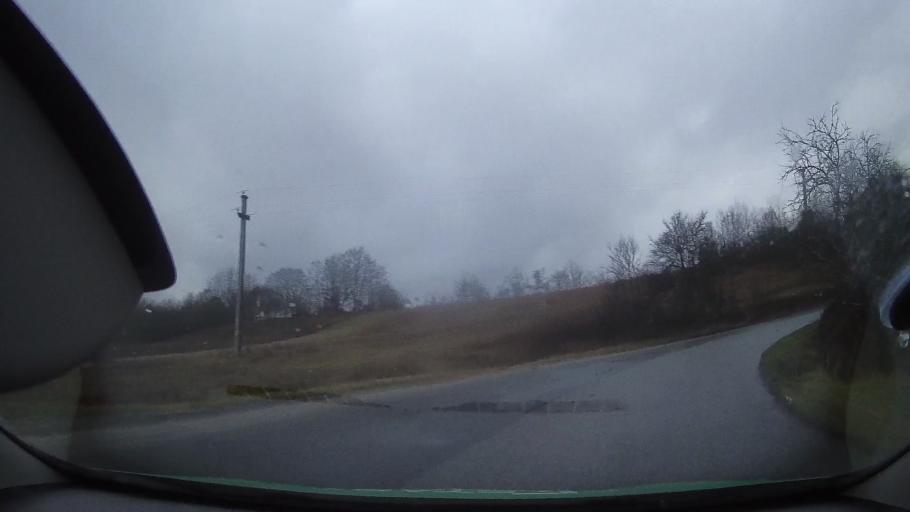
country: RO
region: Hunedoara
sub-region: Comuna Ribita
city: Ribita
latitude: 46.2297
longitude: 22.7341
